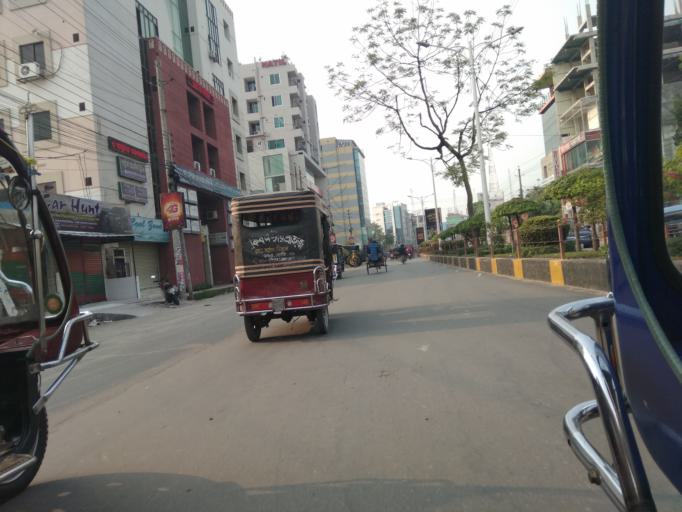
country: BD
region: Khulna
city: Khulna
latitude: 22.8158
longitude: 89.5542
